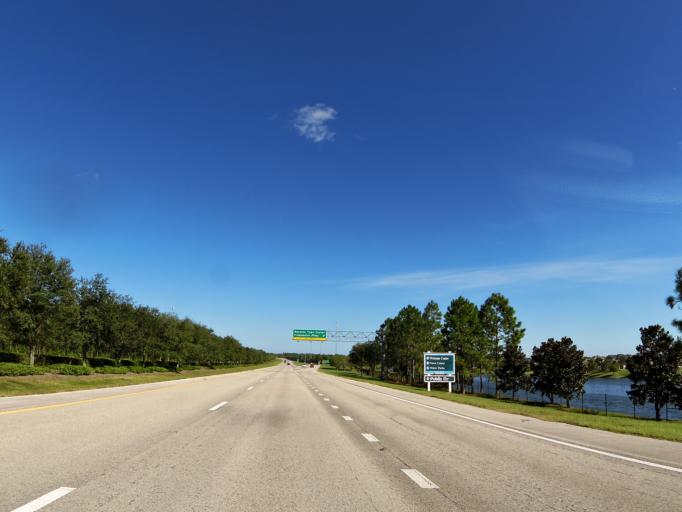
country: US
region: Florida
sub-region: Saint Johns County
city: Palm Valley
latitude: 30.1145
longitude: -81.4289
